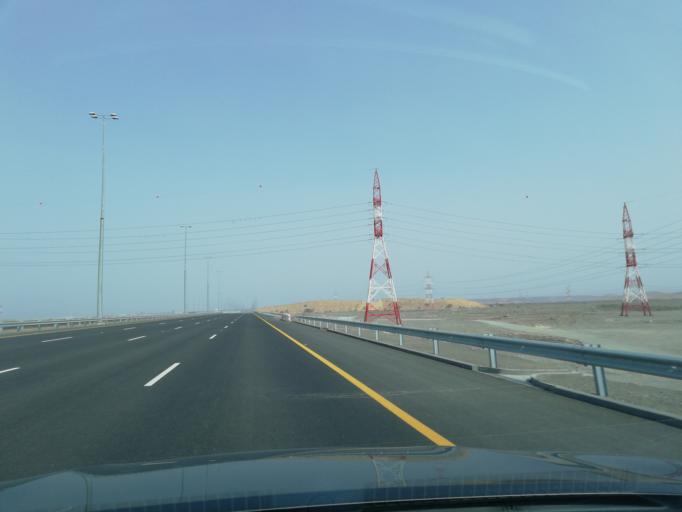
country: OM
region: Al Batinah
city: Al Sohar
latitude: 24.3269
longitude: 56.5644
